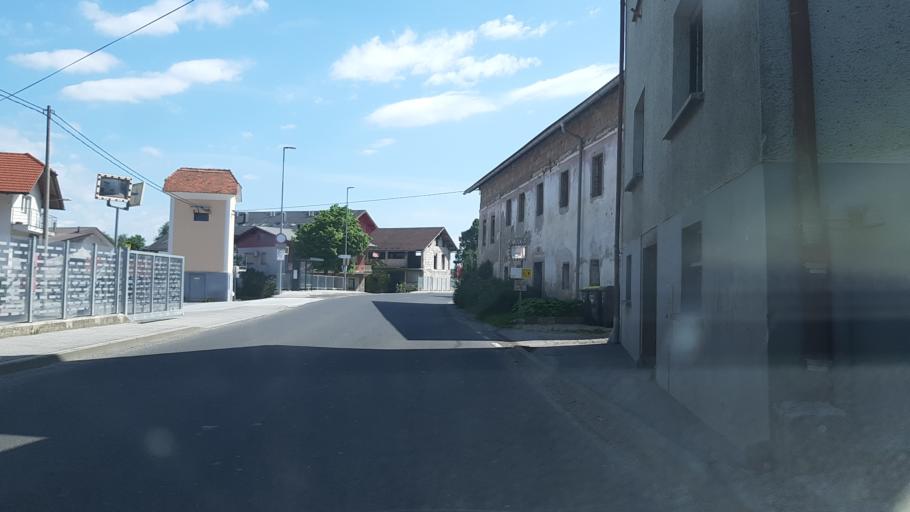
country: SI
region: Brezovica
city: Notranje Gorice
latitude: 45.9728
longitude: 14.4191
